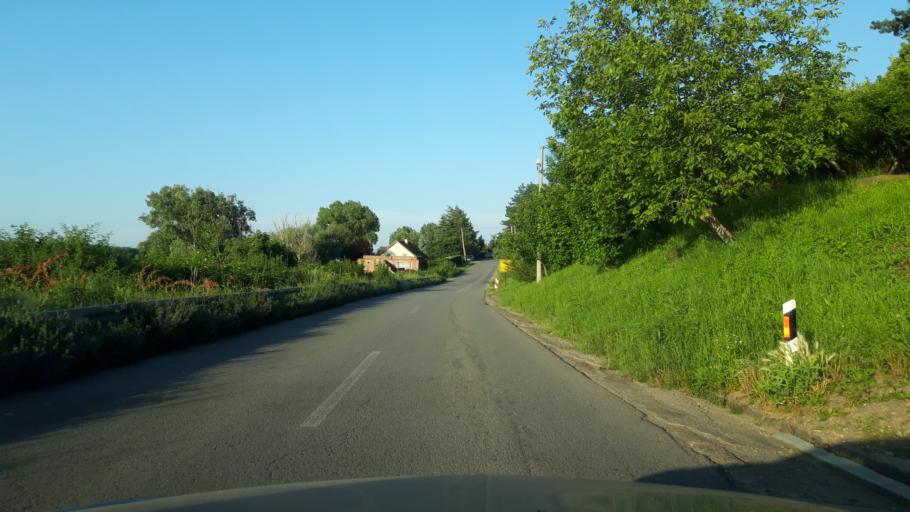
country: RS
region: Autonomna Pokrajina Vojvodina
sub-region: Juznobacki Okrug
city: Beocin
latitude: 45.2195
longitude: 19.6495
